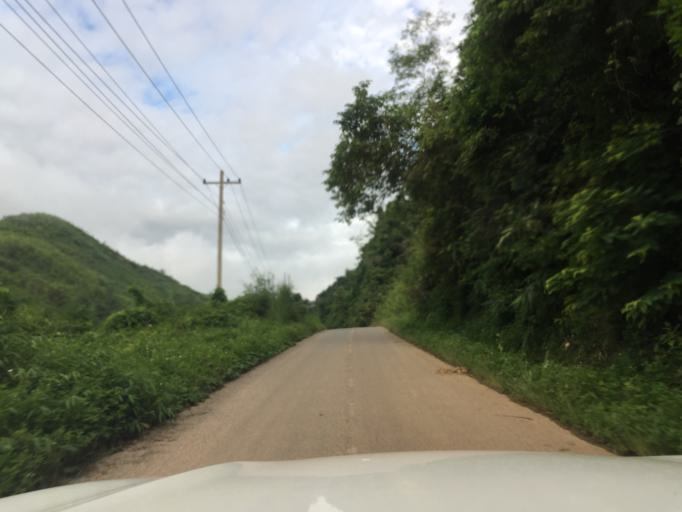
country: LA
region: Phongsali
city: Khoa
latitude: 21.1034
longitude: 102.2956
